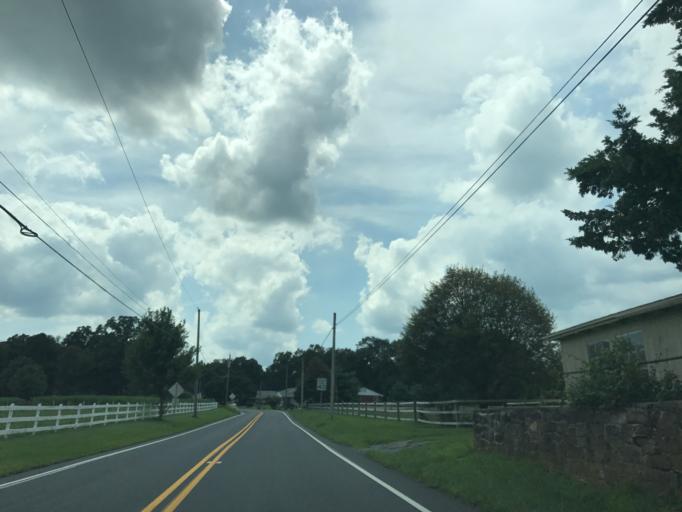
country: US
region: Pennsylvania
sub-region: Lancaster County
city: Manheim
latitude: 40.1908
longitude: -76.4544
